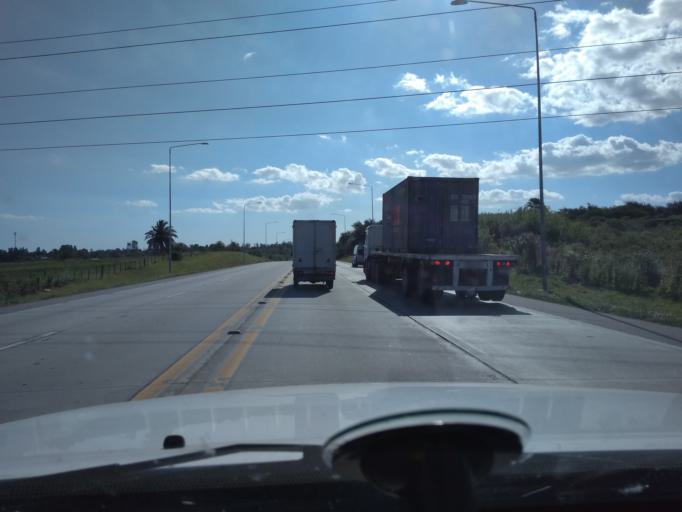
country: UY
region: Canelones
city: La Paz
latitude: -34.7803
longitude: -56.2375
